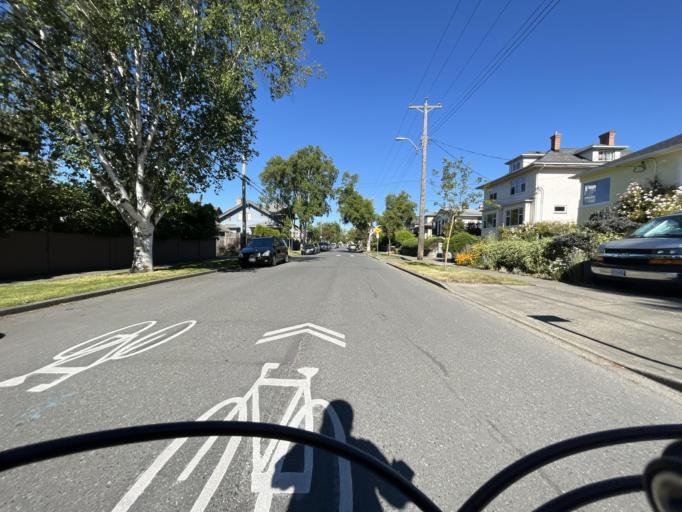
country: CA
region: British Columbia
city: Victoria
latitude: 48.4193
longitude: -123.3519
